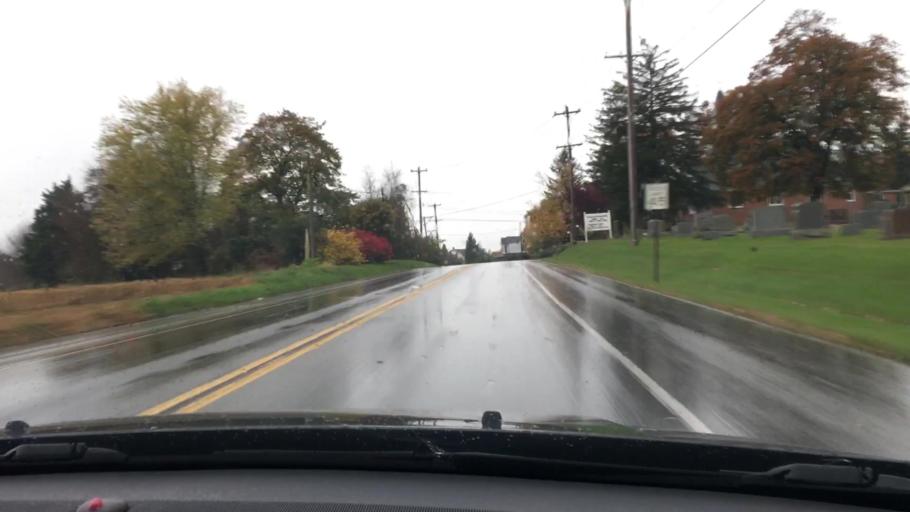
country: US
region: Pennsylvania
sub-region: York County
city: Susquehanna Trails
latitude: 39.8033
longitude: -76.3685
